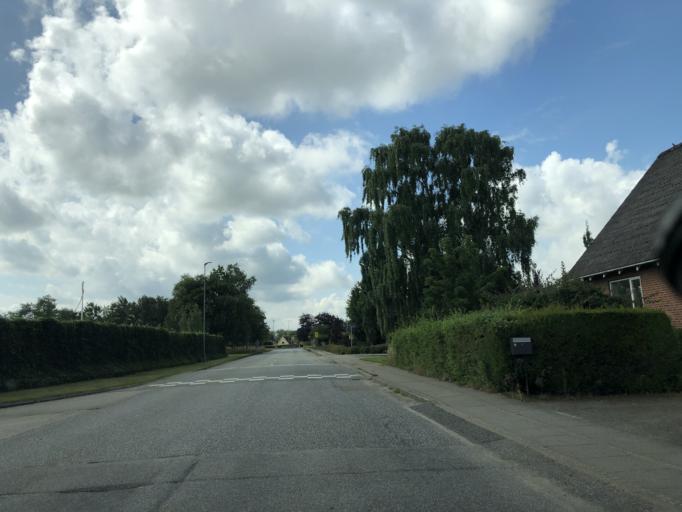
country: DK
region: Central Jutland
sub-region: Ikast-Brande Kommune
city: Brande
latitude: 55.9466
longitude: 9.1376
